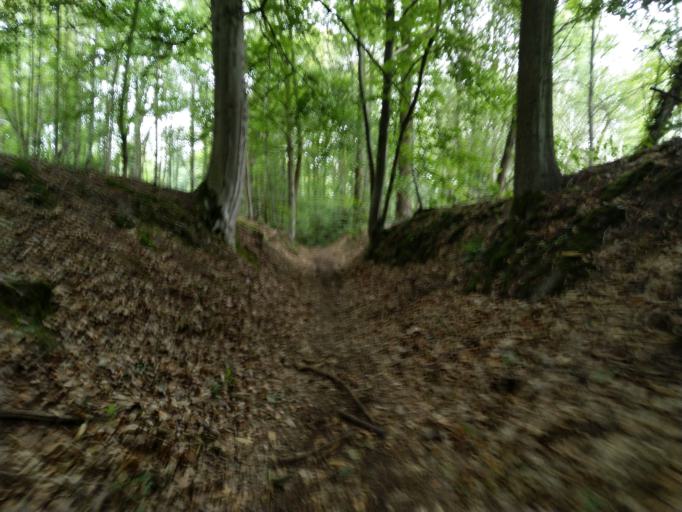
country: BE
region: Wallonia
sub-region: Province du Hainaut
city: Mons
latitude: 50.4984
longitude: 3.9494
